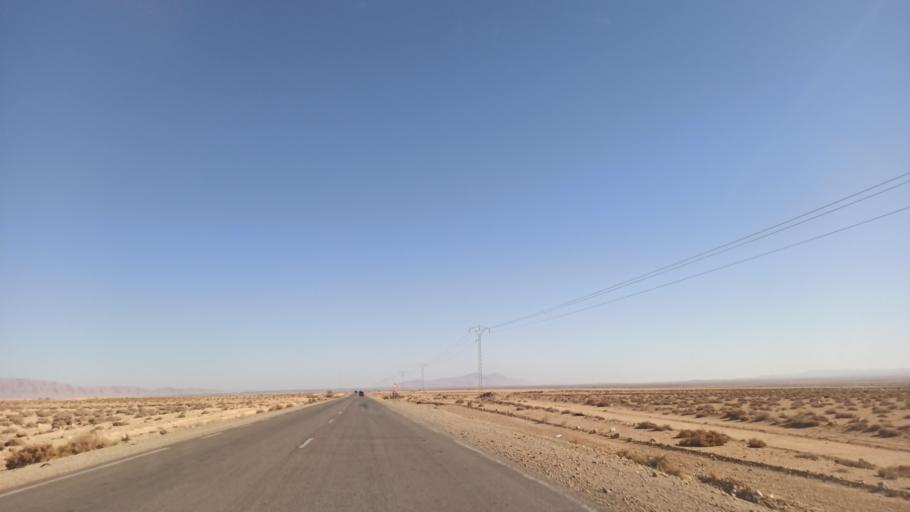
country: TN
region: Gafsa
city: Al Metlaoui
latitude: 34.3223
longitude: 8.5254
